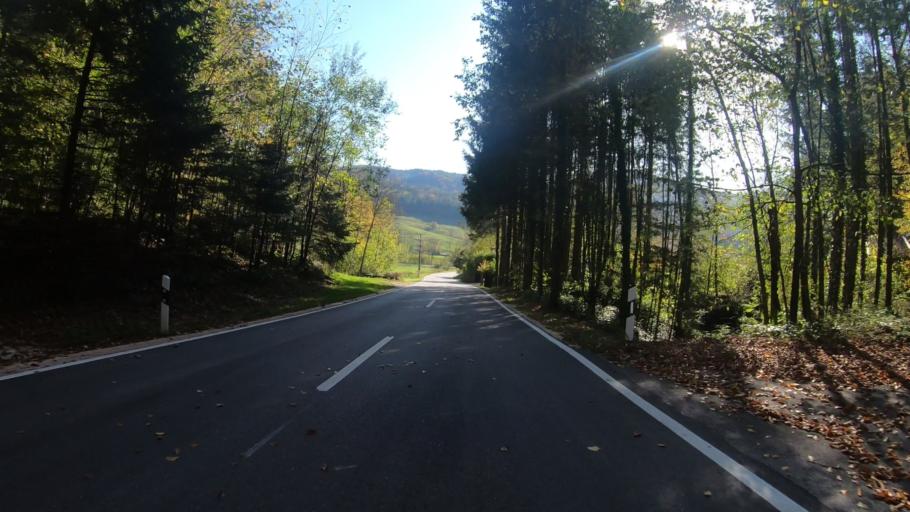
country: DE
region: Bavaria
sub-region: Upper Bavaria
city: Bergen
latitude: 47.8083
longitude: 12.6132
